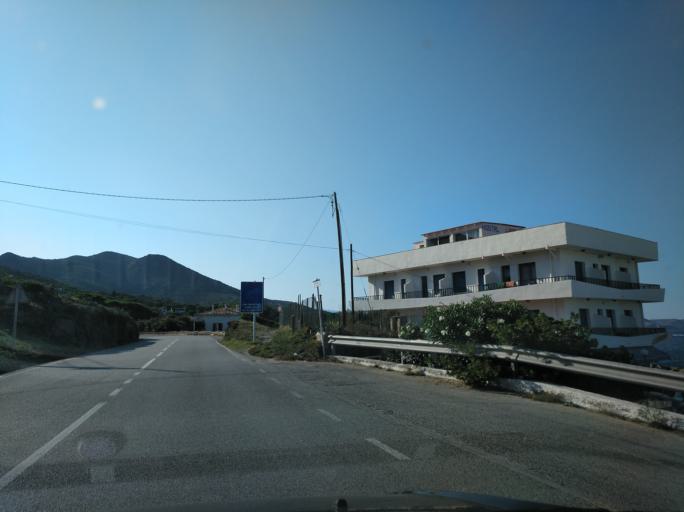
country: ES
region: Catalonia
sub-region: Provincia de Girona
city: Llanca
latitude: 42.3343
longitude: 3.1972
